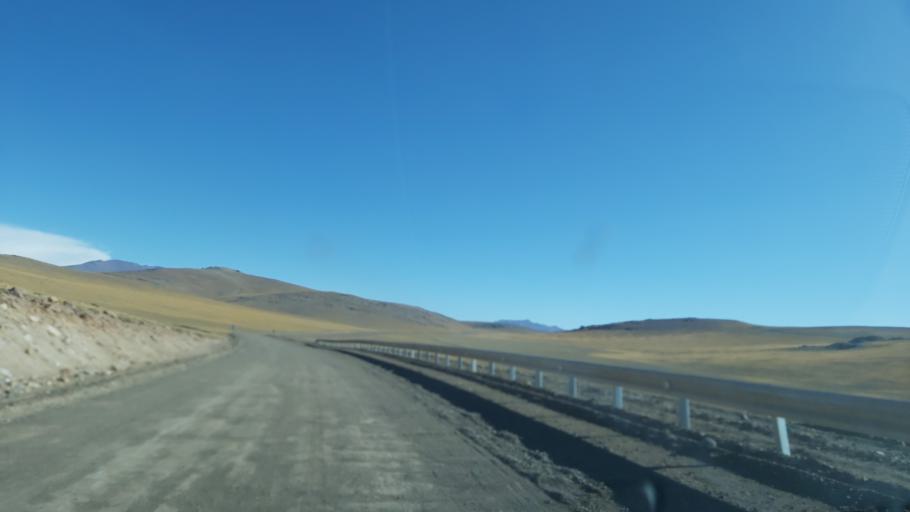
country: CL
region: Atacama
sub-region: Provincia de Chanaral
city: Diego de Almagro
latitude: -26.4514
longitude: -69.2900
